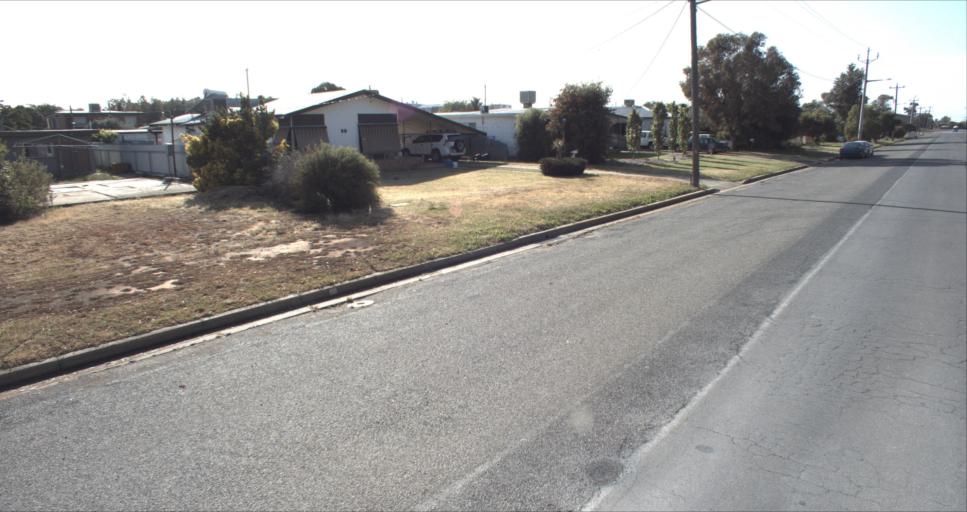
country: AU
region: New South Wales
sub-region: Leeton
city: Leeton
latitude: -34.5560
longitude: 146.3888
